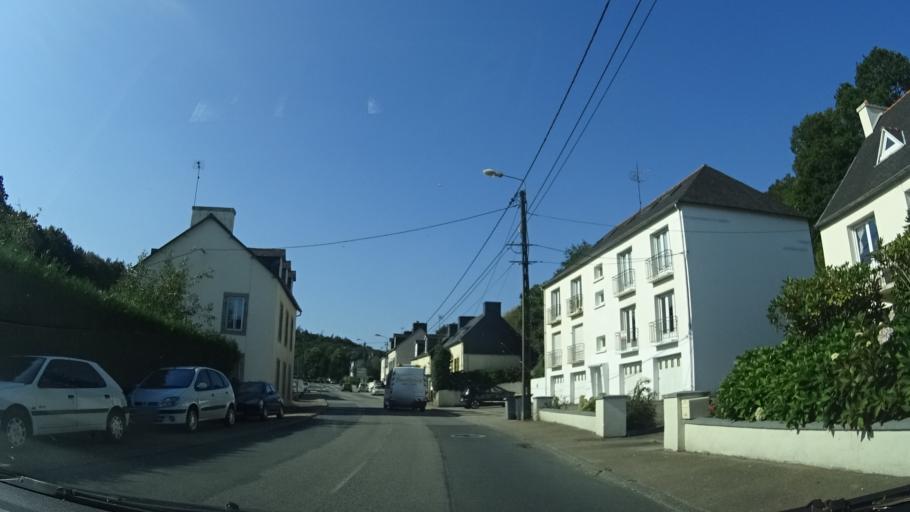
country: FR
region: Brittany
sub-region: Departement du Finistere
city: Chateaulin
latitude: 48.1938
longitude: -4.1065
